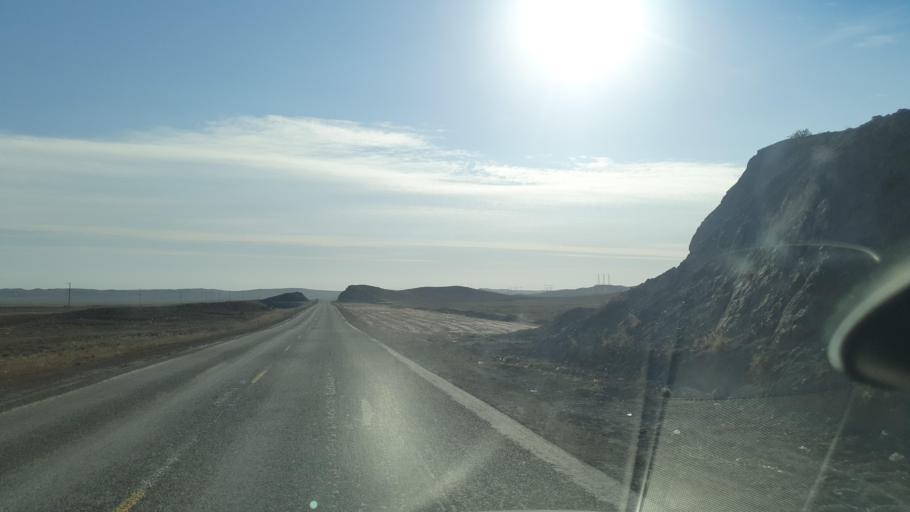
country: KZ
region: Zhambyl
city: Mynaral
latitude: 45.6989
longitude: 73.3993
